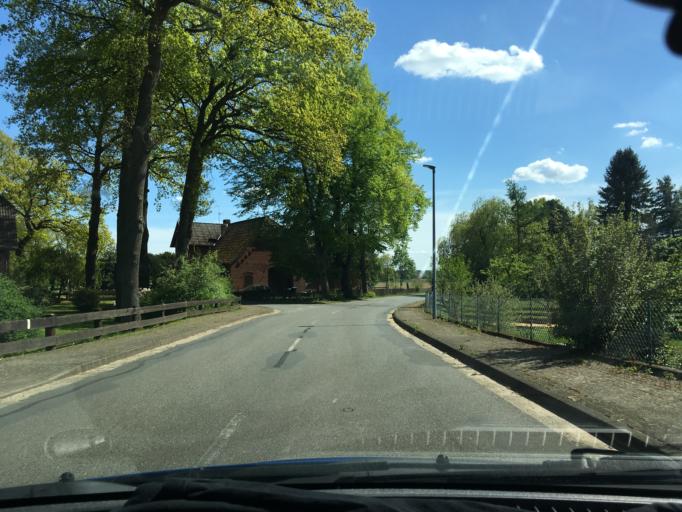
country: DE
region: Lower Saxony
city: Zernien
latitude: 53.0335
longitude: 10.8877
